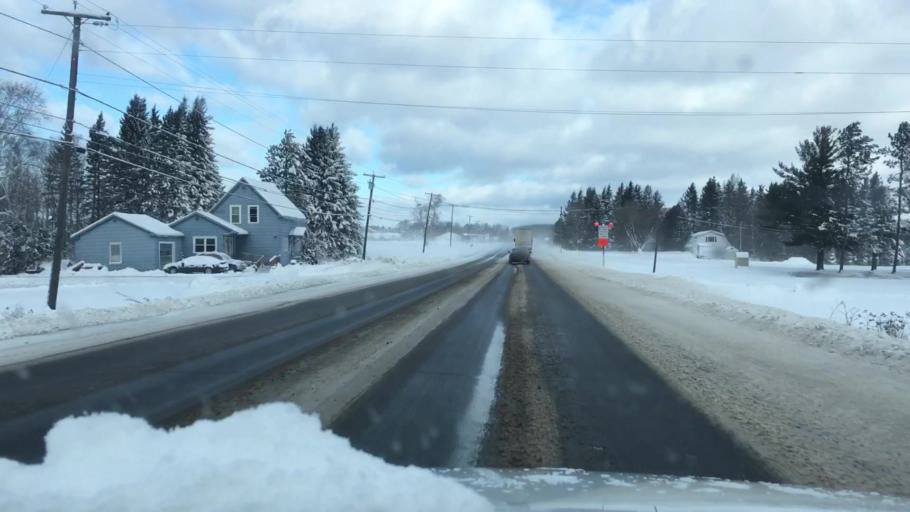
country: US
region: Maine
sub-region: Aroostook County
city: Caribou
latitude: 46.8062
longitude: -67.9938
